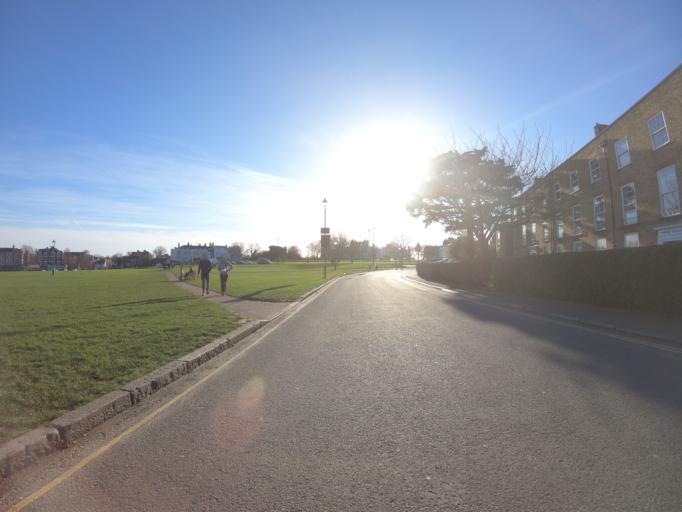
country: GB
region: England
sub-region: Greater London
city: Blackheath
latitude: 51.4688
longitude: 0.0052
